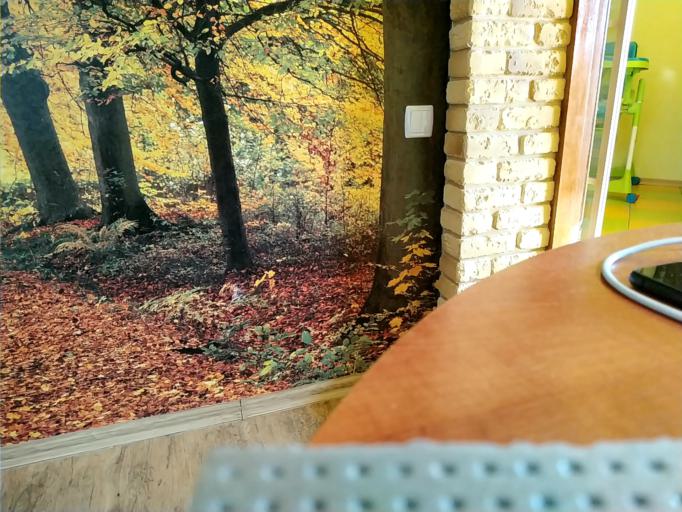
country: RU
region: Tverskaya
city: Kalashnikovo
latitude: 57.3474
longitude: 35.2106
